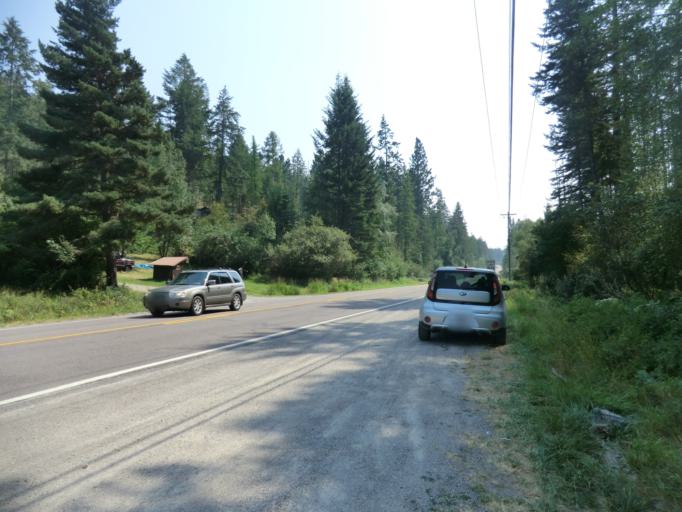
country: US
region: Montana
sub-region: Flathead County
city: Bigfork
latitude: 48.0362
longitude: -114.0717
